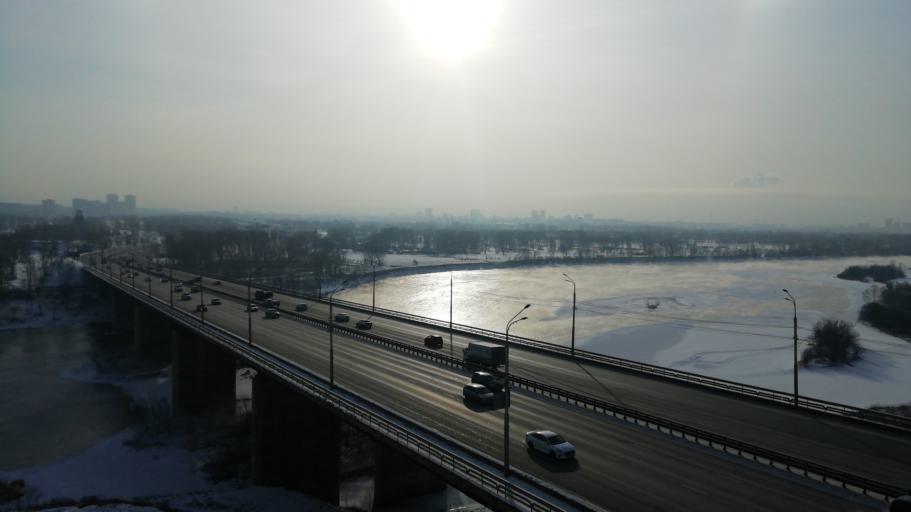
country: RU
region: Krasnoyarskiy
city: Krasnoyarsk
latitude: 56.0362
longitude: 92.9341
